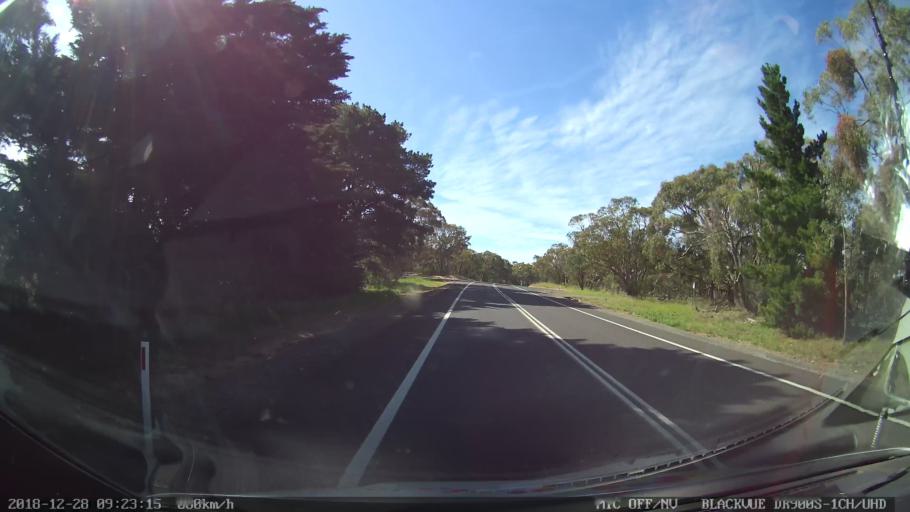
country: AU
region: New South Wales
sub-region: Upper Lachlan Shire
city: Crookwell
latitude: -34.3833
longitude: 149.3837
